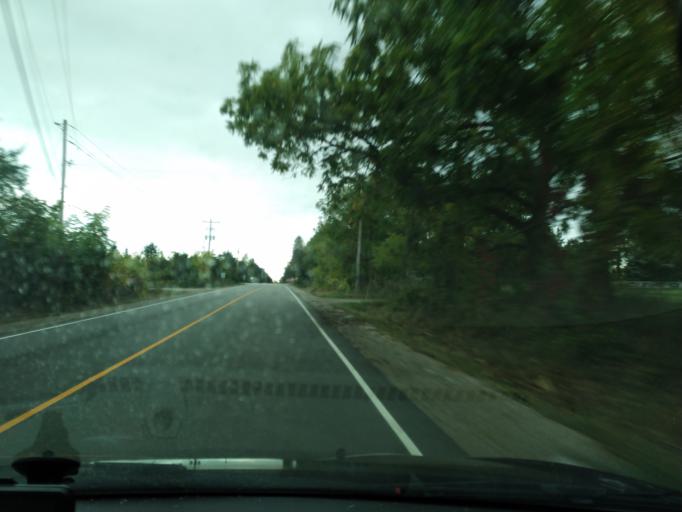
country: CA
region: Ontario
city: Bradford West Gwillimbury
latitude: 44.1394
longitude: -79.5689
